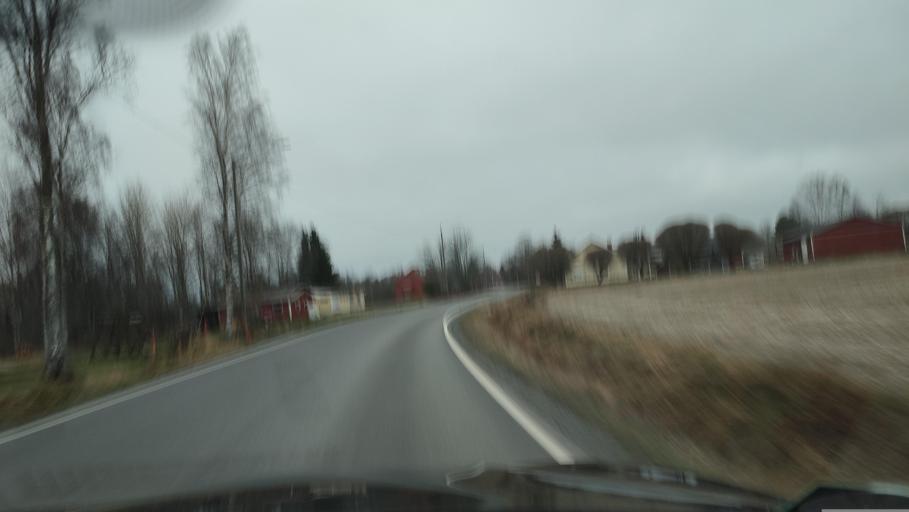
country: FI
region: Southern Ostrobothnia
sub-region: Suupohja
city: Karijoki
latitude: 62.2755
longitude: 21.7073
